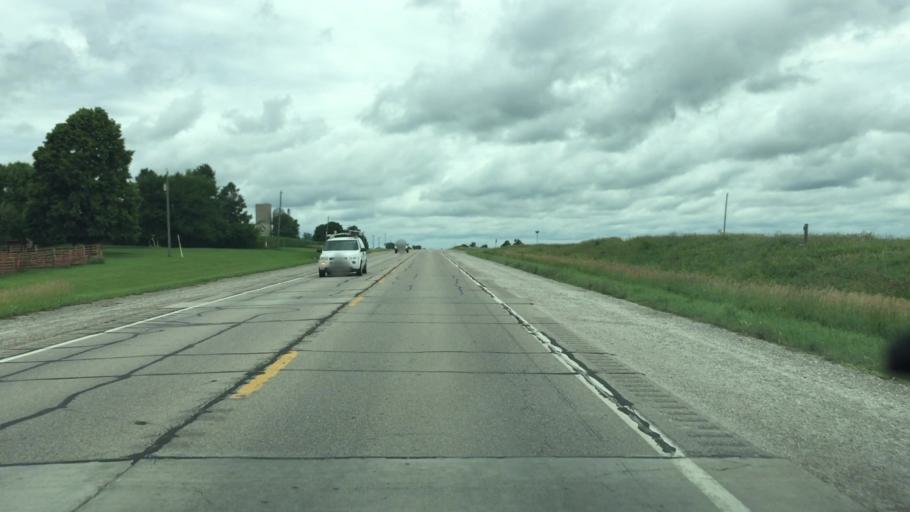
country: US
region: Iowa
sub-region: Jasper County
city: Monroe
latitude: 41.5504
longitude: -93.0970
